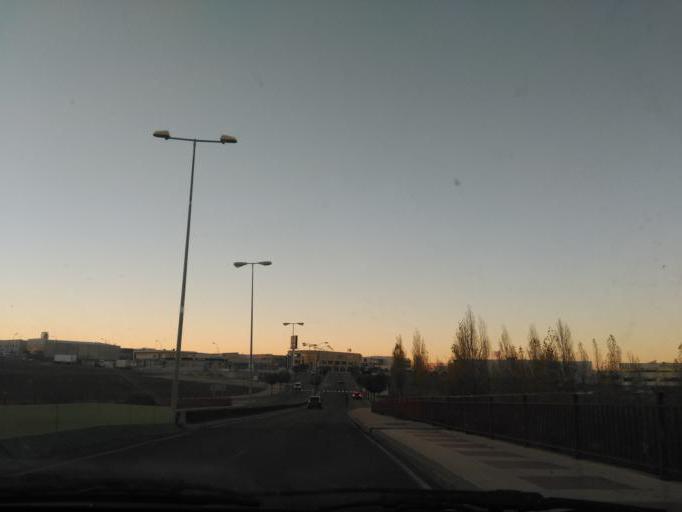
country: ES
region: Castille and Leon
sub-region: Provincia de Salamanca
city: Carbajosa de la Sagrada
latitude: 40.9377
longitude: -5.6524
